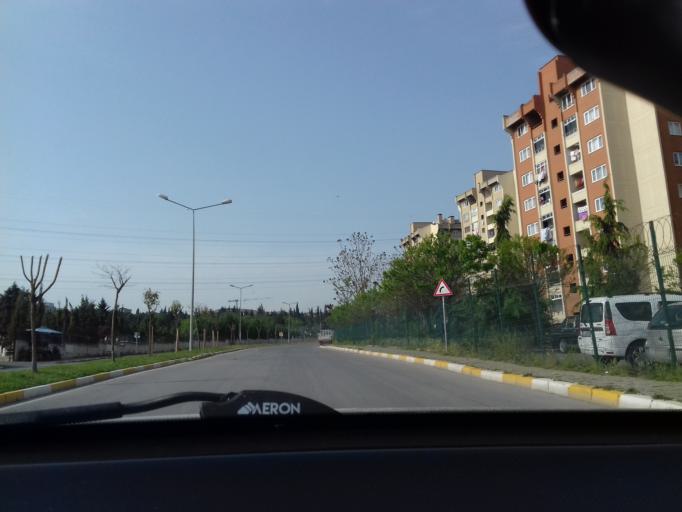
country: TR
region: Istanbul
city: Pendik
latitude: 40.9072
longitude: 29.2754
